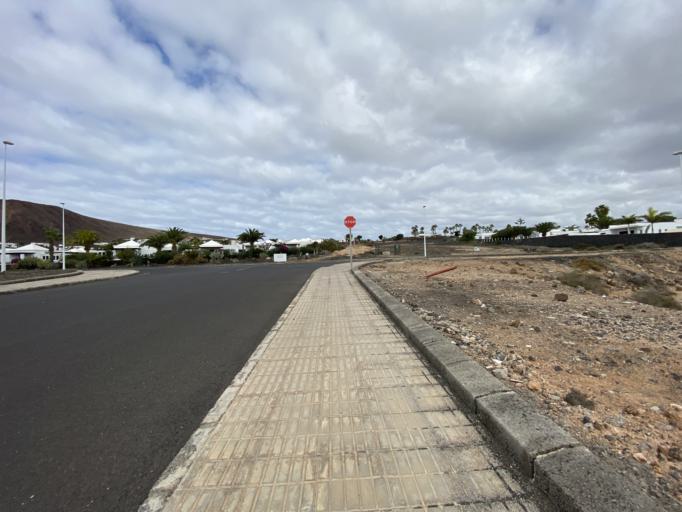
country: ES
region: Canary Islands
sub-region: Provincia de Las Palmas
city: Playa Blanca
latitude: 28.8636
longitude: -13.8461
